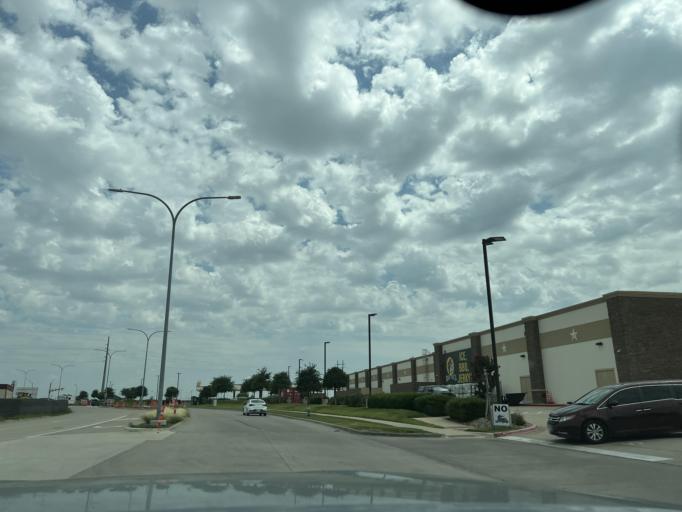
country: US
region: Texas
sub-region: Denton County
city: Roanoke
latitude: 33.0238
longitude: -97.2794
